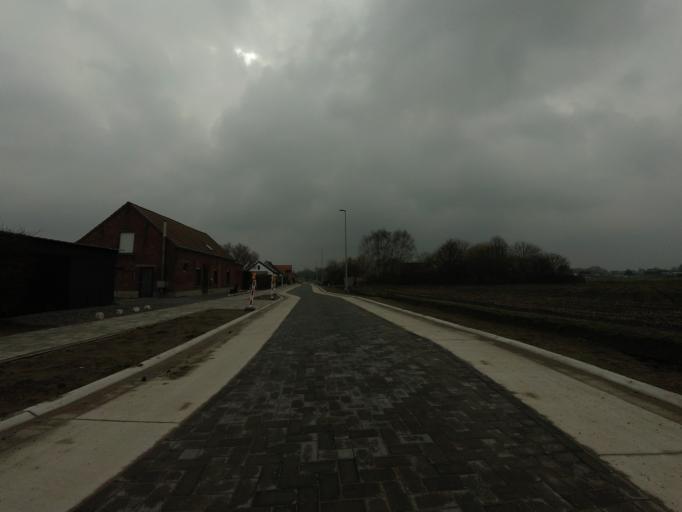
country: BE
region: Flanders
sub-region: Provincie Antwerpen
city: Sint-Katelijne-Waver
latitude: 51.0608
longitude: 4.5687
